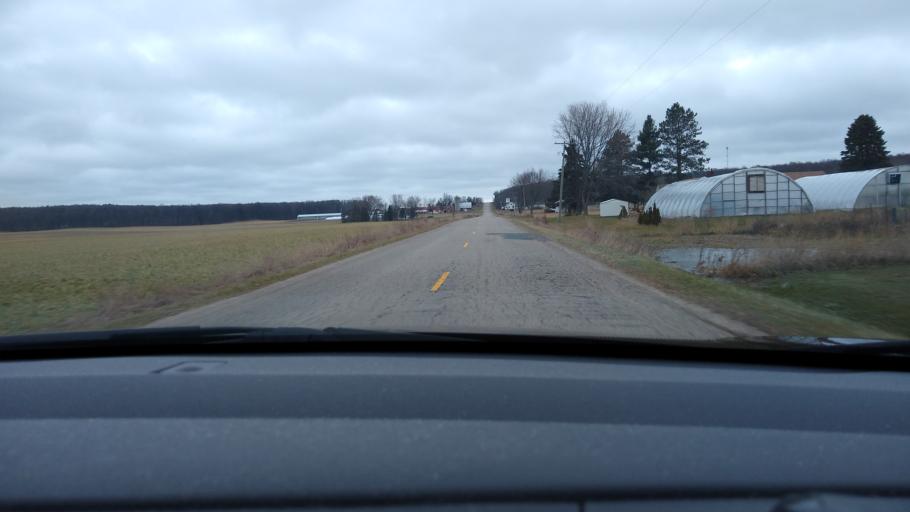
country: US
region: Michigan
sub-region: Missaukee County
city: Lake City
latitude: 44.2798
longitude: -85.0541
